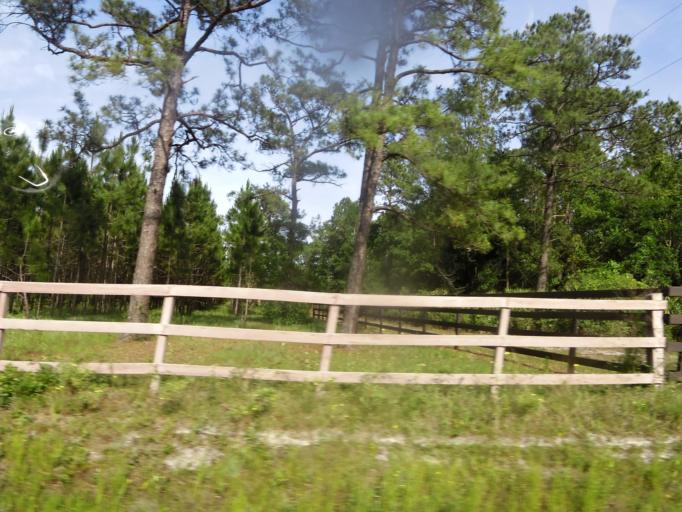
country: US
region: Florida
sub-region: Duval County
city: Atlantic Beach
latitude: 30.4897
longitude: -81.4720
